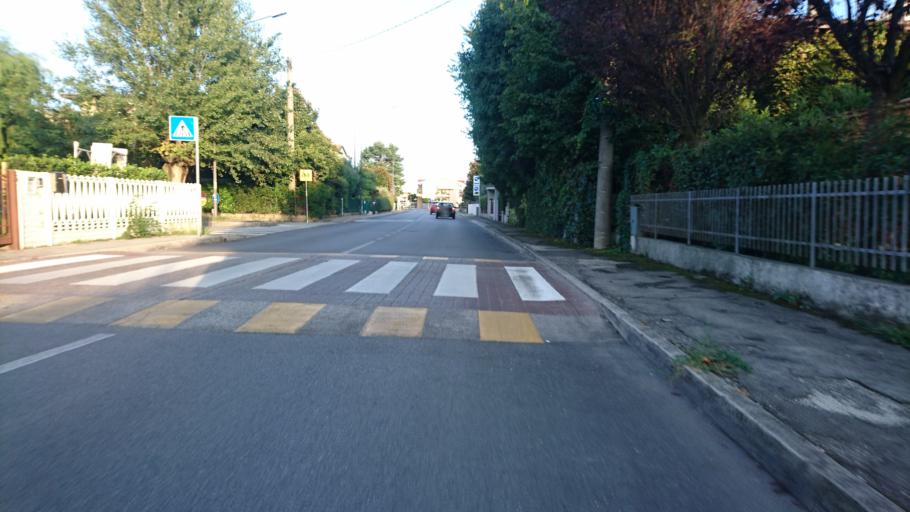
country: IT
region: Veneto
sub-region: Provincia di Padova
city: Montegrotto Terme
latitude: 45.3414
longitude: 11.7749
